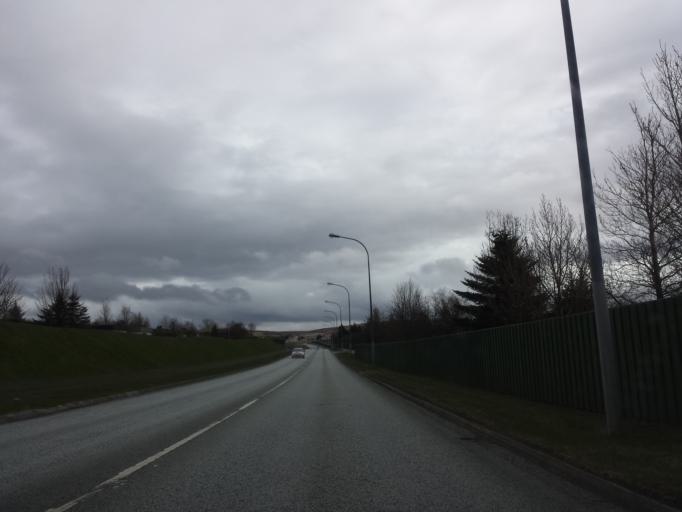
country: IS
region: Capital Region
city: Gardabaer
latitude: 64.0846
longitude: -21.9069
